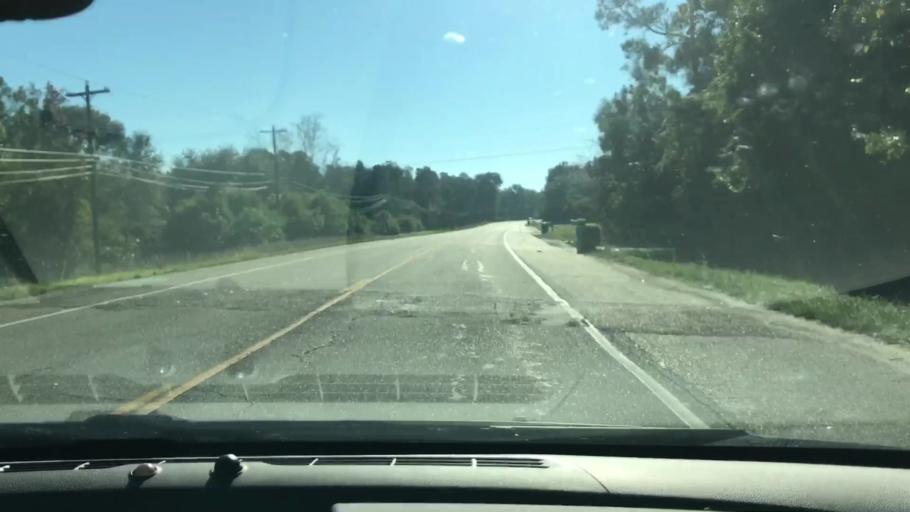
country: US
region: Louisiana
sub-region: Saint Tammany Parish
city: Pearl River
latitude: 30.4416
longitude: -89.7914
